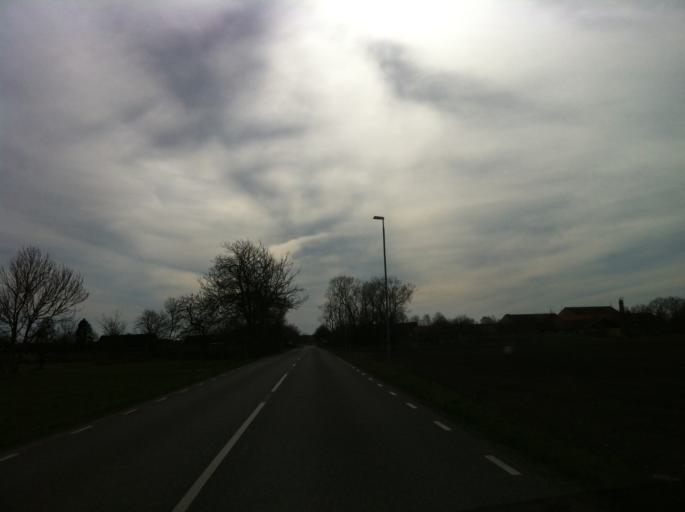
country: SE
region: Skane
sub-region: Hoganas Kommun
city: Hoganas
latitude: 56.2452
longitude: 12.5455
